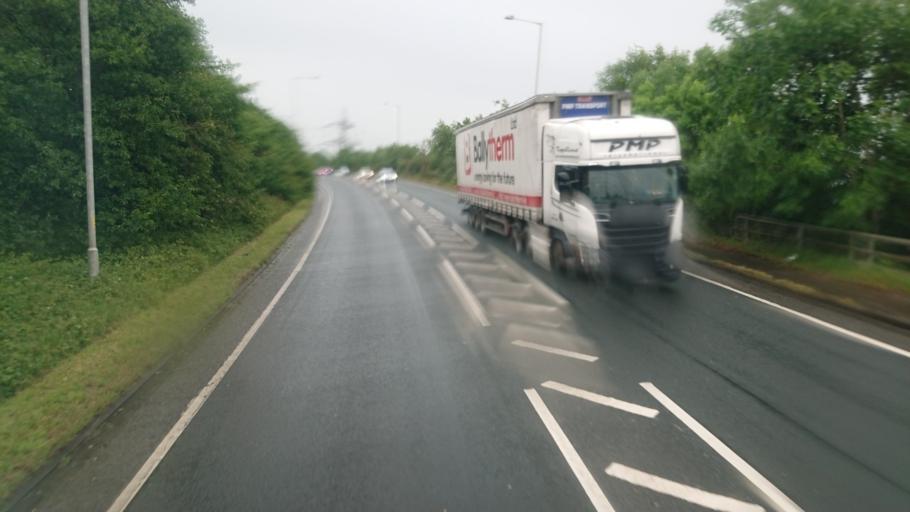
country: GB
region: England
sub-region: Lancashire
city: Morecambe
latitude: 54.0348
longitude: -2.8946
